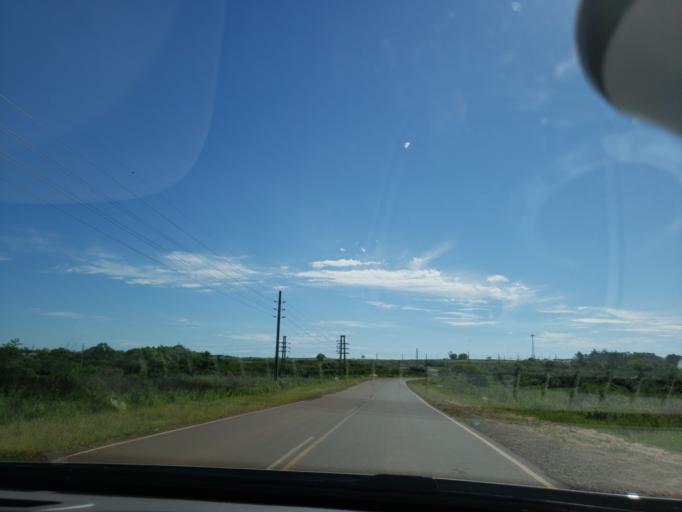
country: AR
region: Misiones
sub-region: Departamento de Capital
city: Posadas
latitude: -27.3900
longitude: -55.9835
